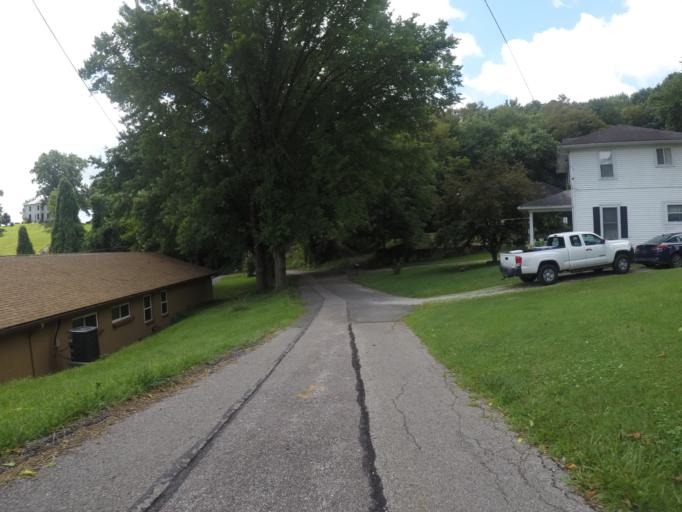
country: US
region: Kentucky
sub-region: Boyd County
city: Catlettsburg
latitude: 38.4054
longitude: -82.6033
